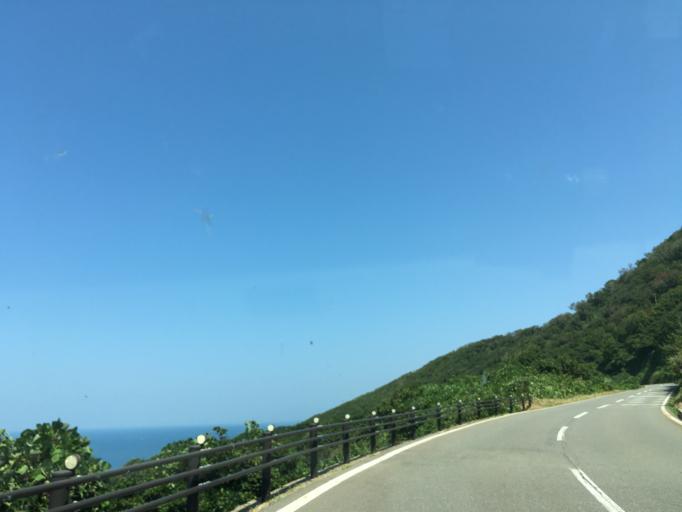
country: JP
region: Akita
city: Tenno
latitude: 39.9325
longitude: 139.7086
